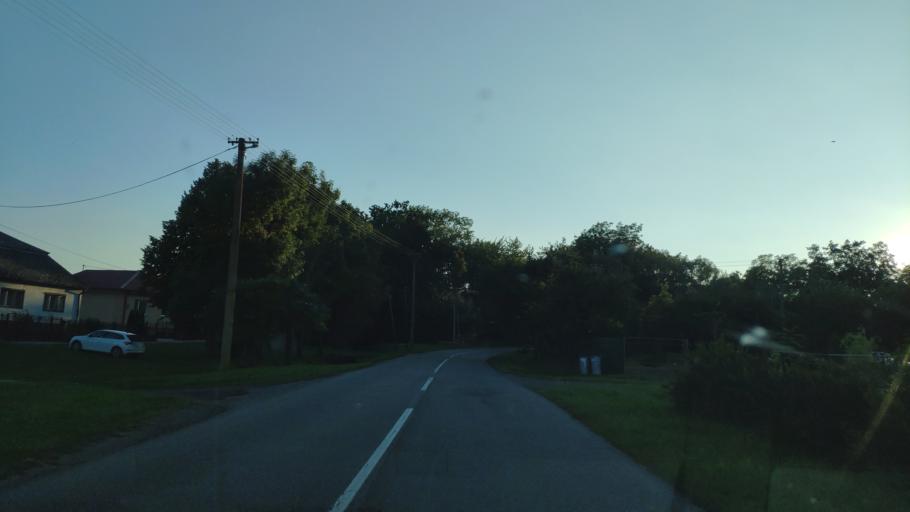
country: SK
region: Kosicky
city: Secovce
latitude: 48.7374
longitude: 21.6156
